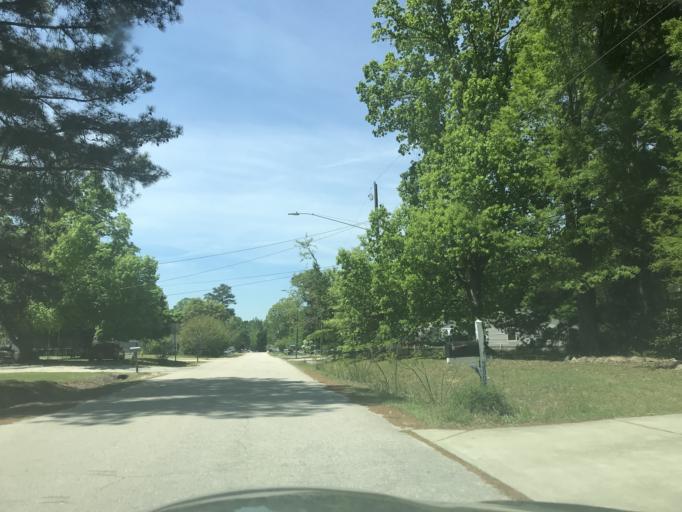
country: US
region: North Carolina
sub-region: Wake County
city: Raleigh
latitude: 35.8257
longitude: -78.5729
